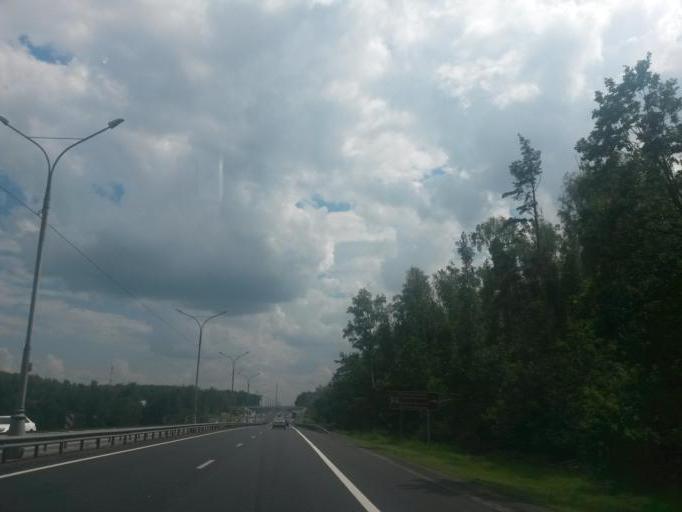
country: RU
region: Moskovskaya
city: Gorki-Leninskiye
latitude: 55.5177
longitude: 37.8254
